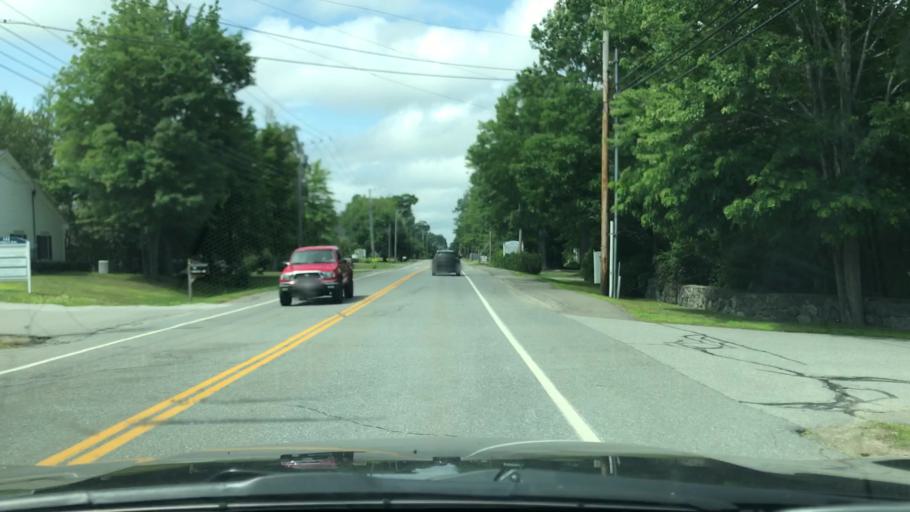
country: US
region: Maine
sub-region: Waldo County
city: Belfast
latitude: 44.4096
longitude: -68.9932
